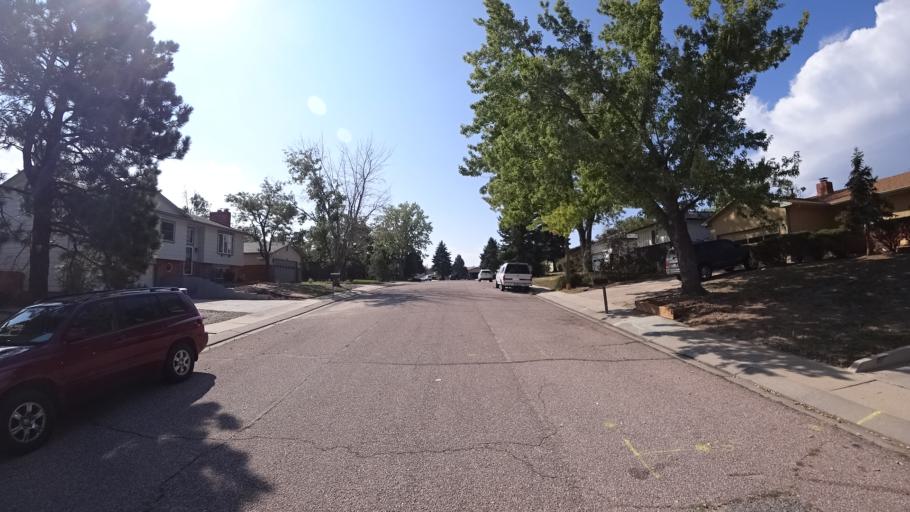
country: US
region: Colorado
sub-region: El Paso County
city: Cimarron Hills
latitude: 38.8672
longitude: -104.7630
